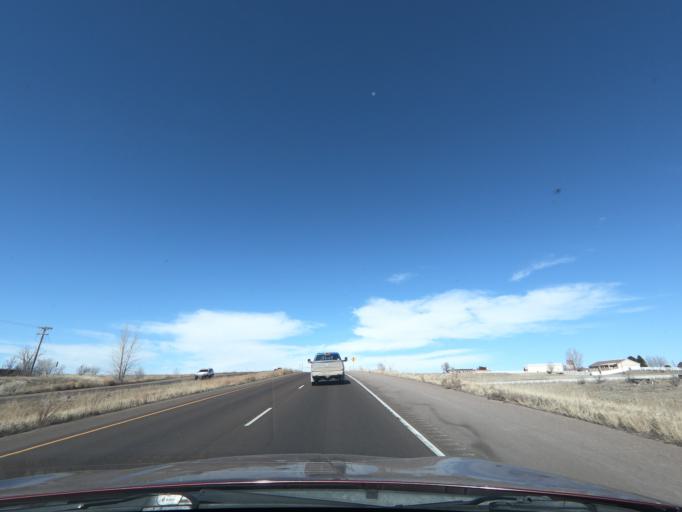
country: US
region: Colorado
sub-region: El Paso County
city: Security-Widefield
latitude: 38.7336
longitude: -104.6822
